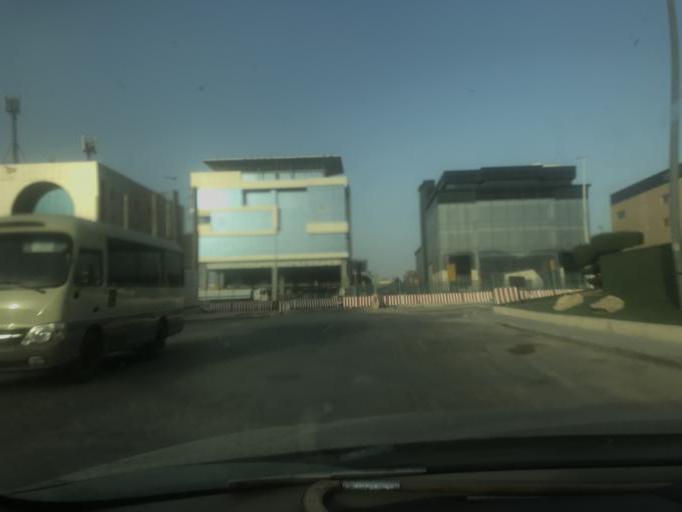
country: SA
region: Ar Riyad
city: Riyadh
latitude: 24.7158
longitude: 46.6733
